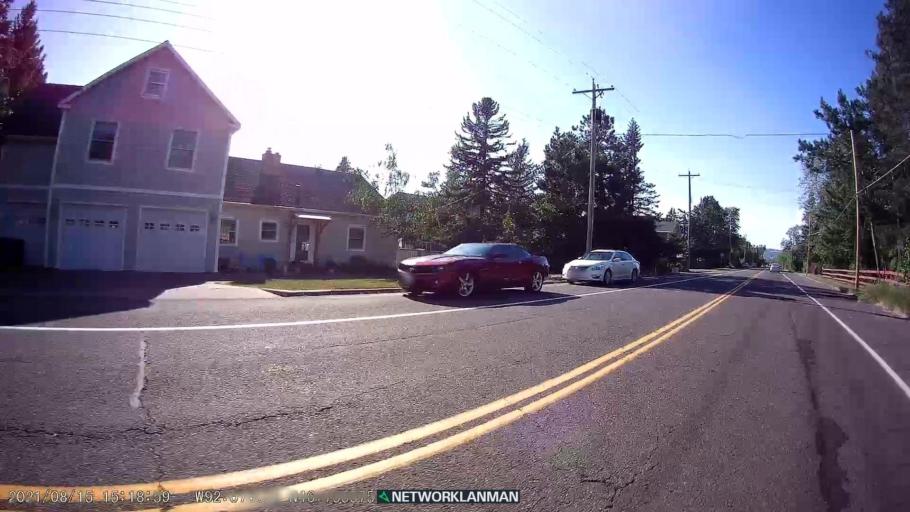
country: US
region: Minnesota
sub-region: Saint Louis County
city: Duluth
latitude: 46.7557
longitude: -92.0761
